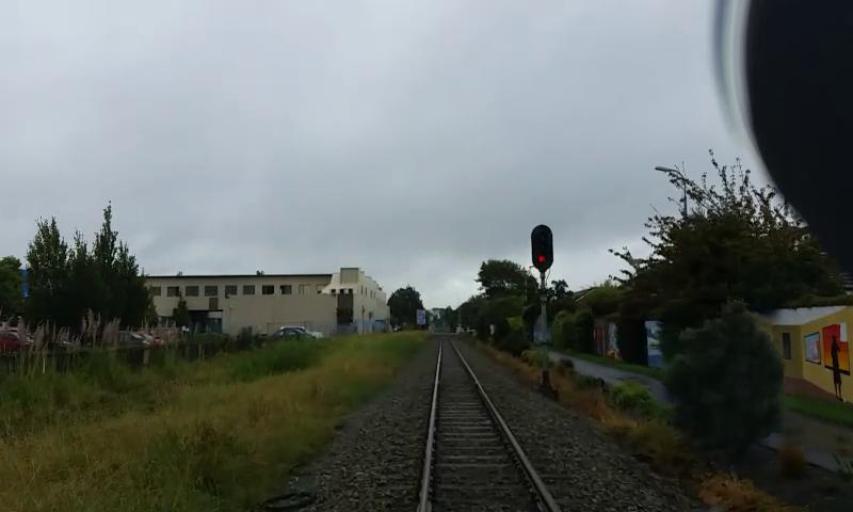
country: NZ
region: Canterbury
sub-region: Christchurch City
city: Christchurch
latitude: -43.5298
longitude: 172.6088
